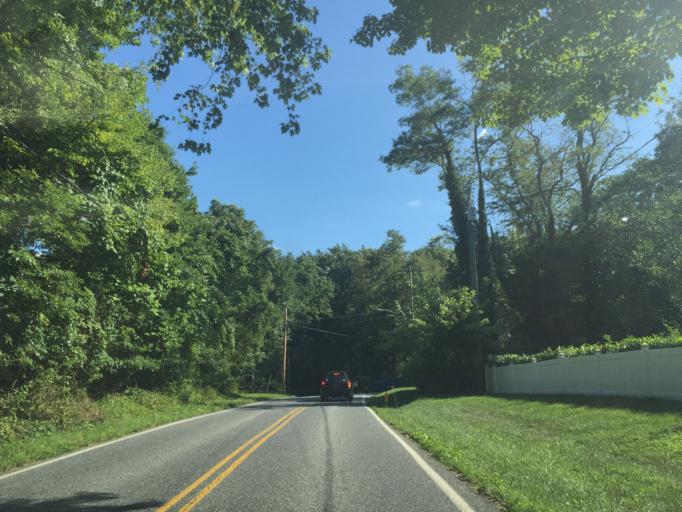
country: US
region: Maryland
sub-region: Harford County
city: Pleasant Hills
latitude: 39.4670
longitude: -76.3819
